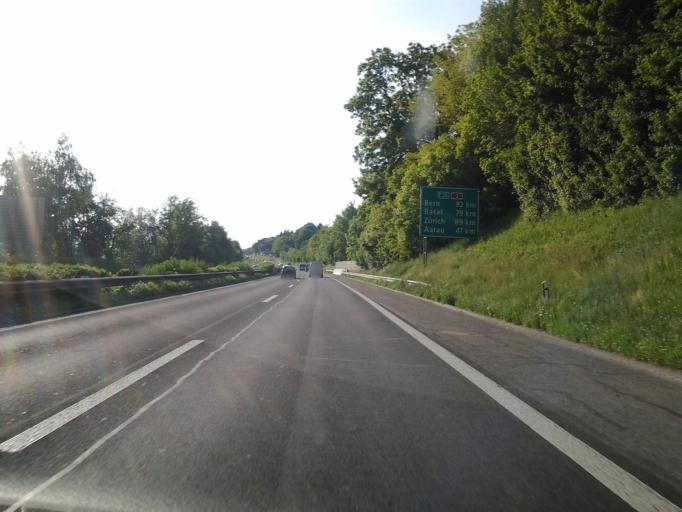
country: CH
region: Lucerne
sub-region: Sursee District
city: Sempach
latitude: 47.1408
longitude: 8.1925
